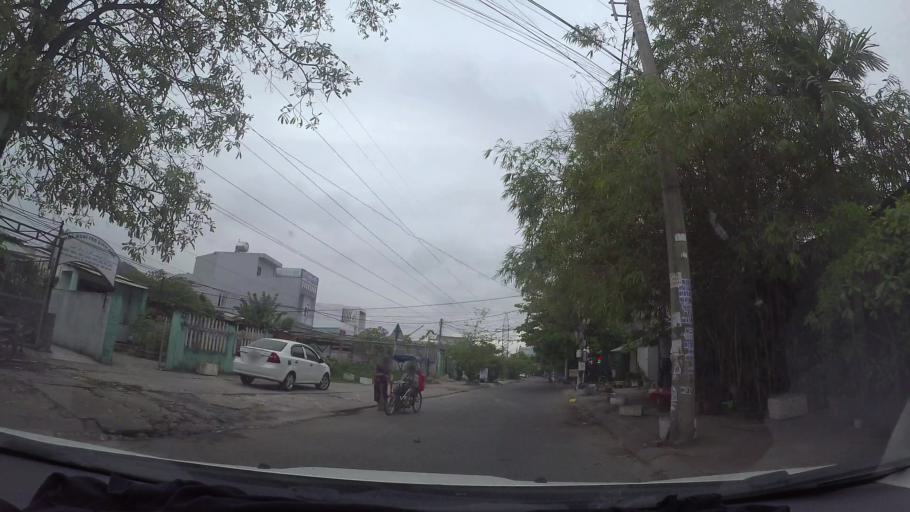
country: VN
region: Da Nang
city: Lien Chieu
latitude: 16.0675
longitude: 108.1475
